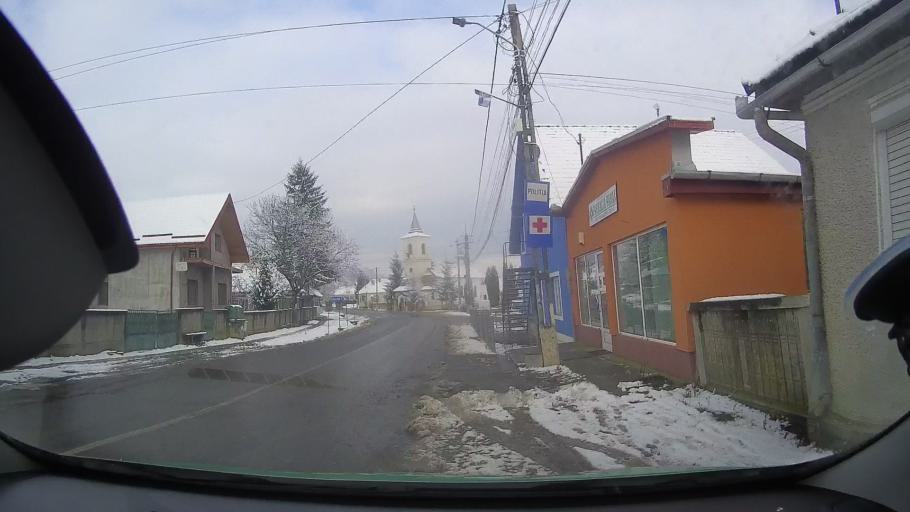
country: RO
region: Mures
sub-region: Comuna Atintis
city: Atintis
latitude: 46.4284
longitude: 24.1046
